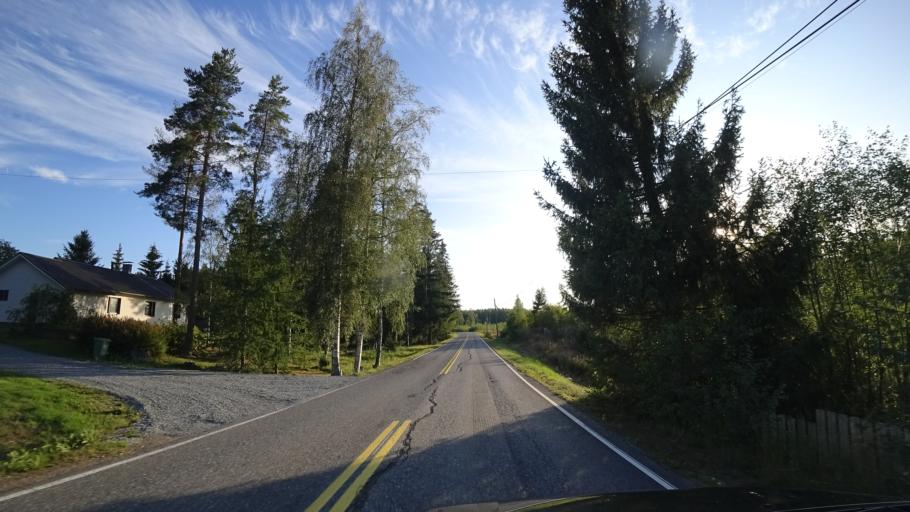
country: FI
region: Haeme
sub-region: Haemeenlinna
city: Lammi
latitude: 61.0495
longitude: 24.9505
